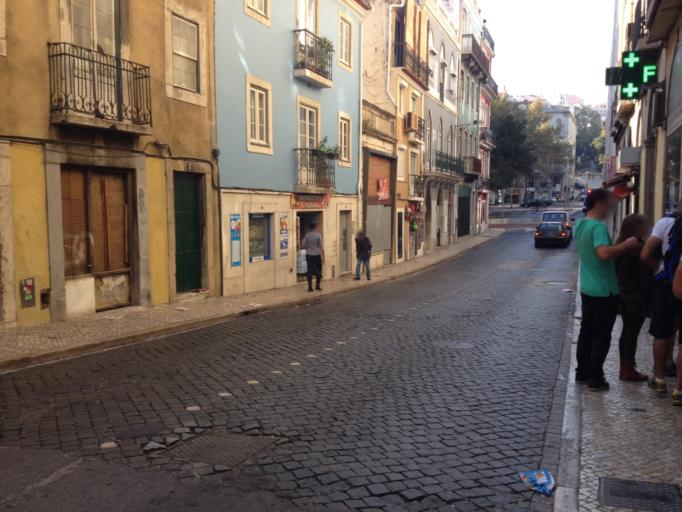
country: PT
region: Lisbon
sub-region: Lisbon
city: Lisbon
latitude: 38.7190
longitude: -9.1431
